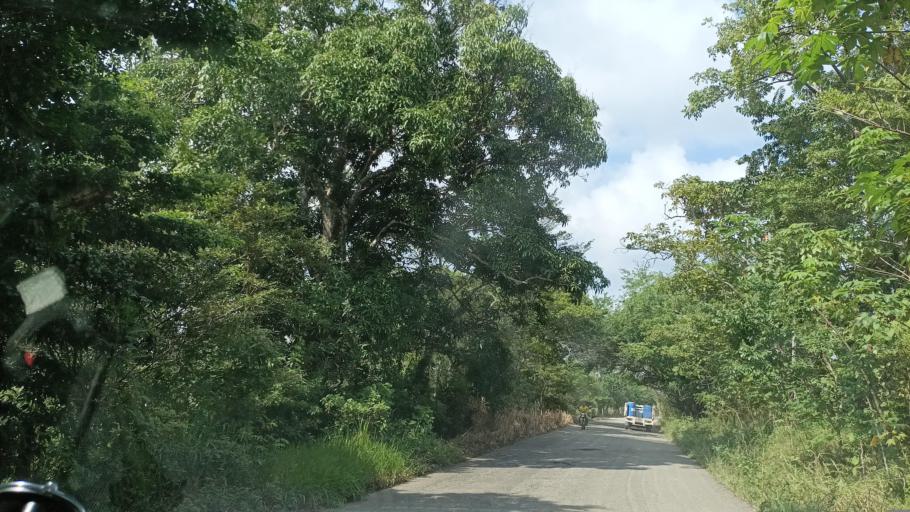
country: MX
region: Veracruz
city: Las Choapas
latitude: 17.7654
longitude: -94.1074
